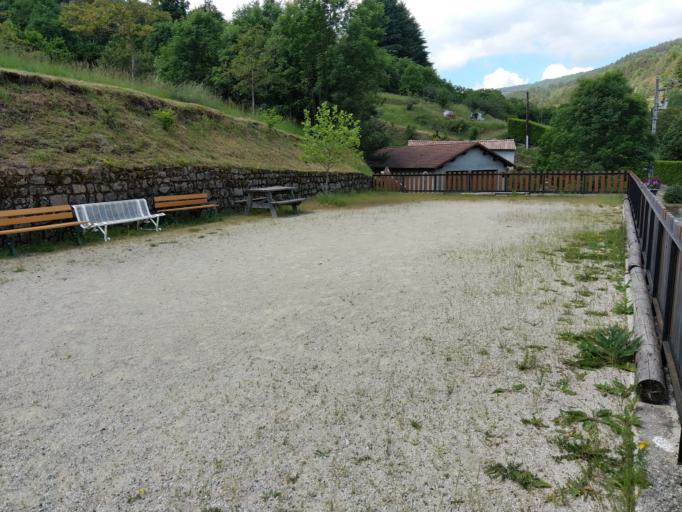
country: FR
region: Rhone-Alpes
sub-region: Departement de l'Ardeche
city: Le Cheylard
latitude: 44.8669
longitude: 4.4416
